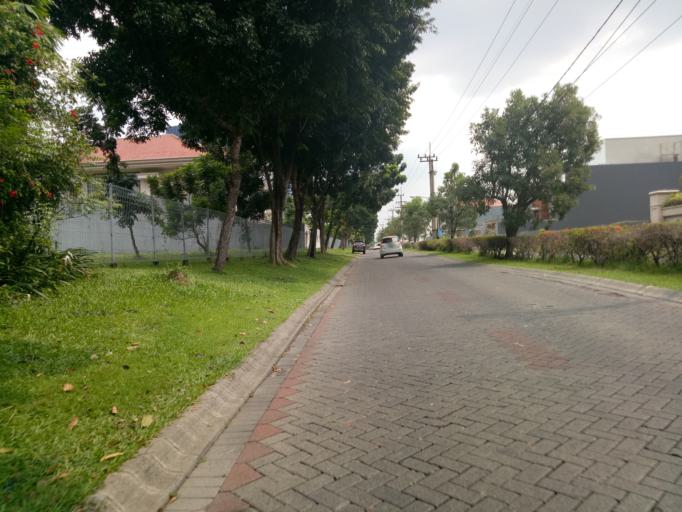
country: ID
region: East Java
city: Jagirsidosermo
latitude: -7.2892
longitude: 112.6815
